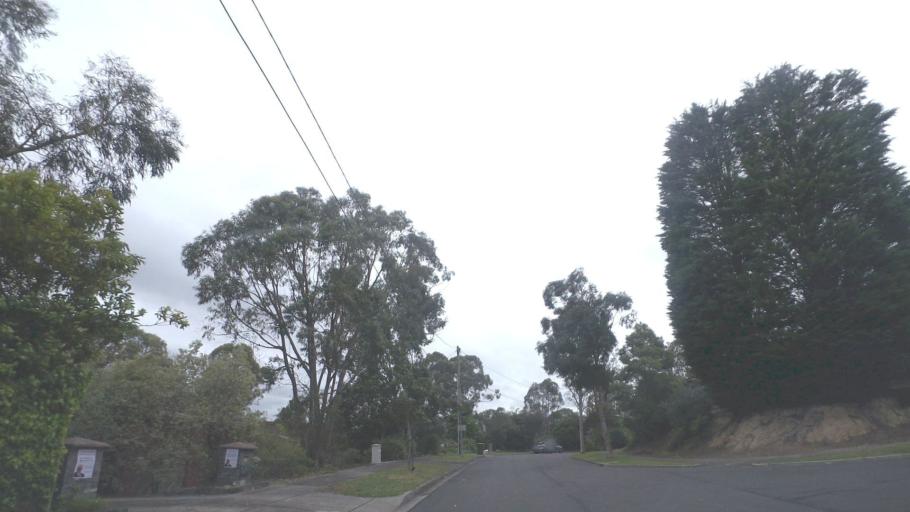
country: AU
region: Victoria
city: Mitcham
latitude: -37.8049
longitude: 145.2013
